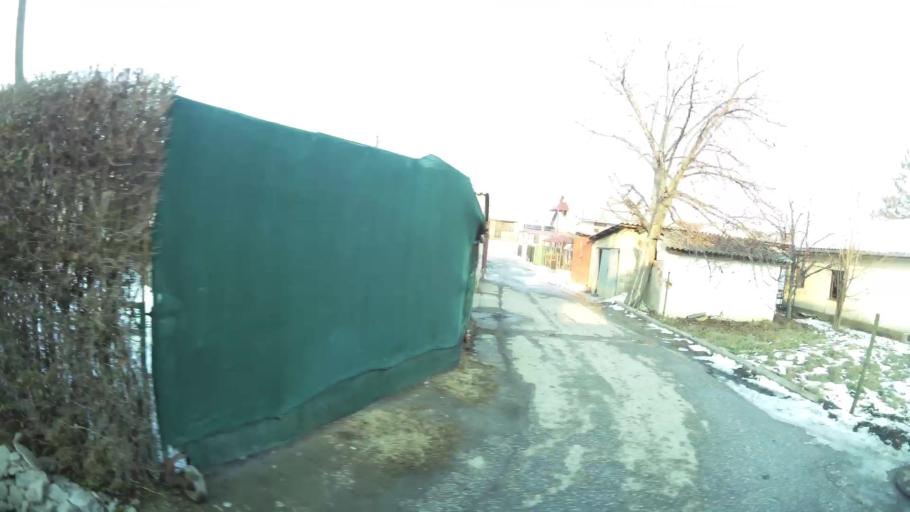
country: MK
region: Aracinovo
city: Arachinovo
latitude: 42.0130
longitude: 21.5274
